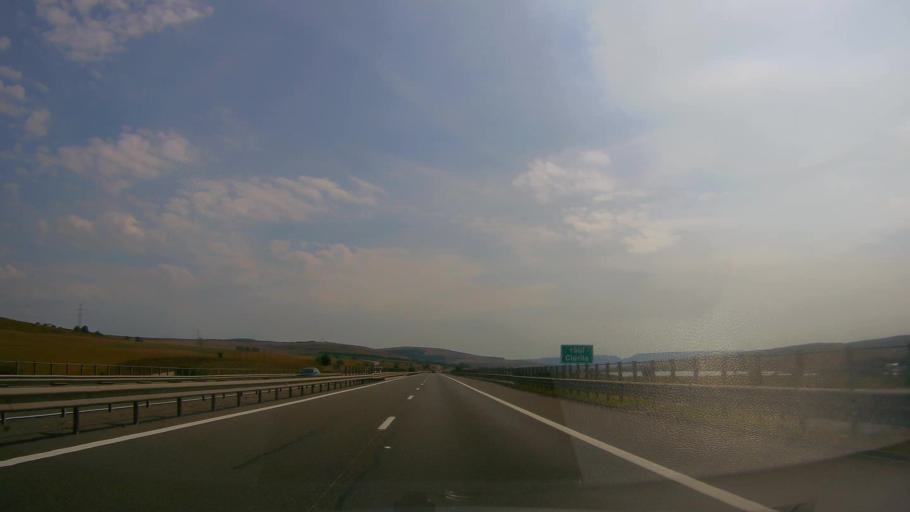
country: RO
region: Cluj
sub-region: Comuna Ciurila
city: Ciurila
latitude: 46.6300
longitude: 23.5523
